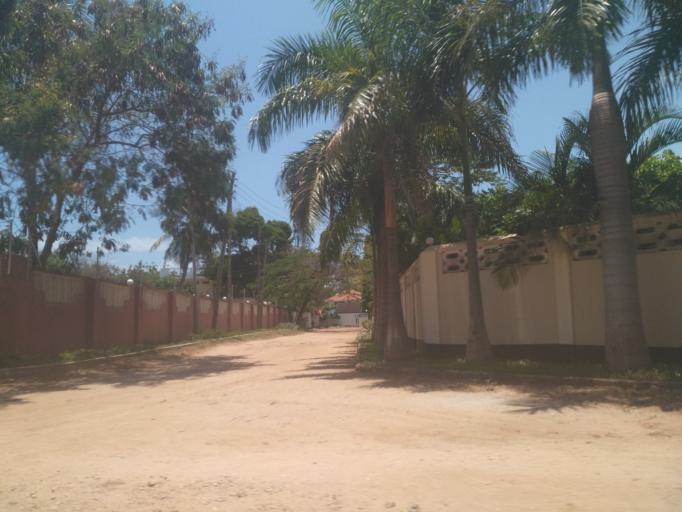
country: TZ
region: Dar es Salaam
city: Magomeni
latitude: -6.7428
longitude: 39.2777
